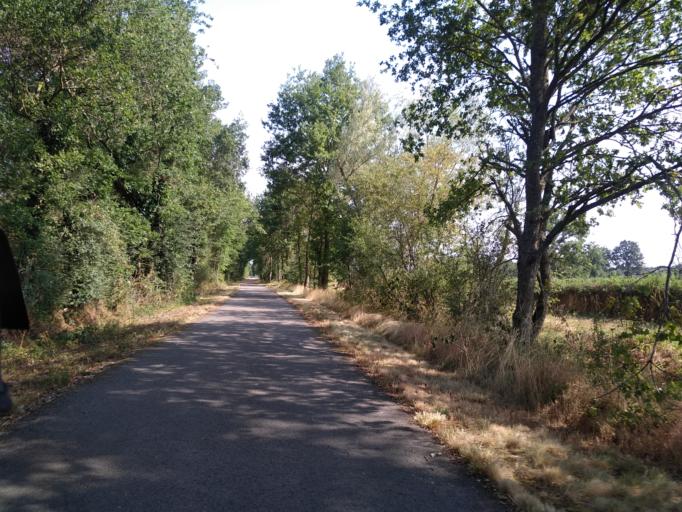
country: FR
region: Bourgogne
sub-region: Departement de Saone-et-Loire
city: Marcigny
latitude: 46.3195
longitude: 4.0284
